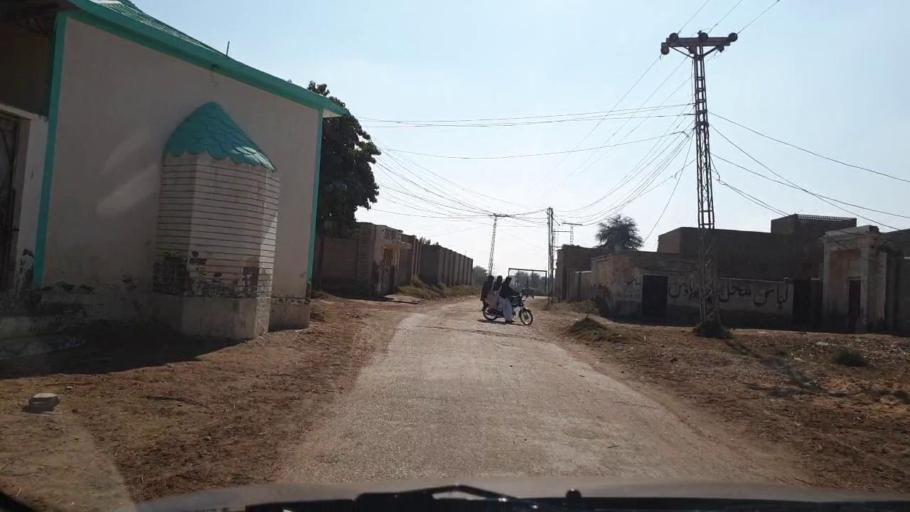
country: PK
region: Sindh
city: Sinjhoro
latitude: 25.9480
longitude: 68.7458
